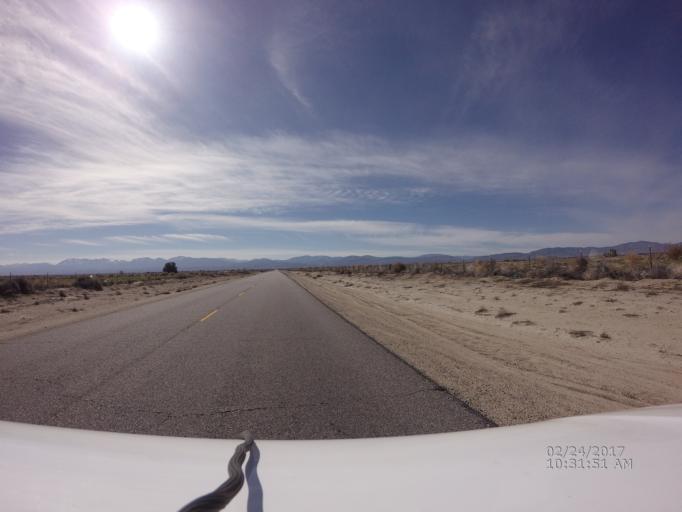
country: US
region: California
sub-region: Los Angeles County
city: Littlerock
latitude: 34.6249
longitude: -118.0053
